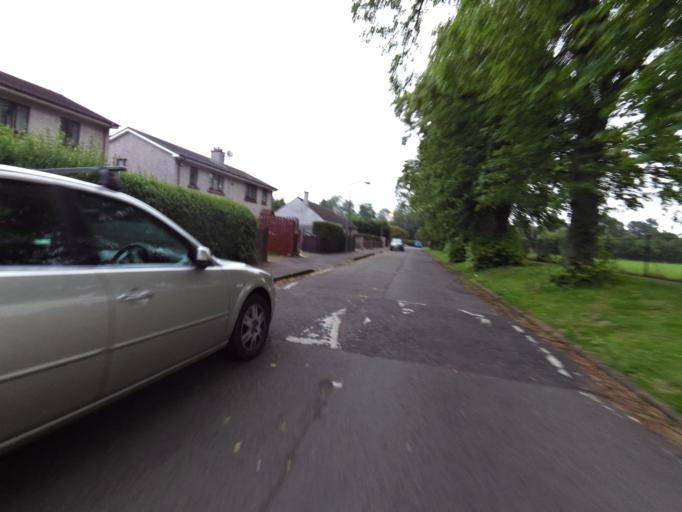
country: GB
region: Scotland
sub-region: Midlothian
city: Loanhead
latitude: 55.9146
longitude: -3.1309
